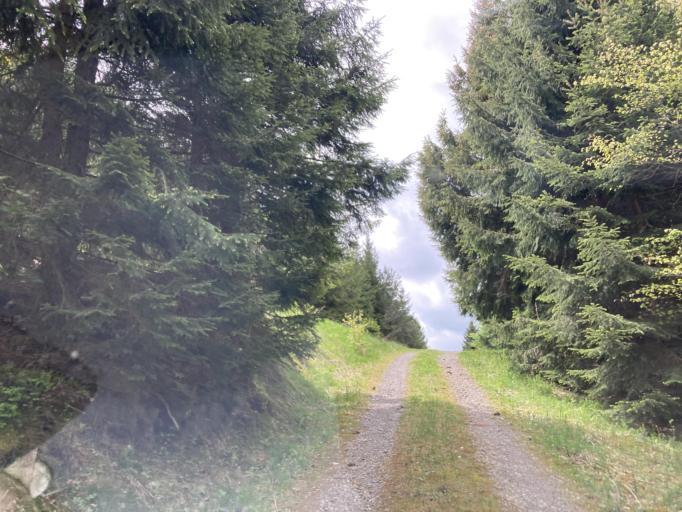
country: DE
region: Baden-Wuerttemberg
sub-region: Karlsruhe Region
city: Biberach
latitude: 48.5246
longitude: 8.2872
